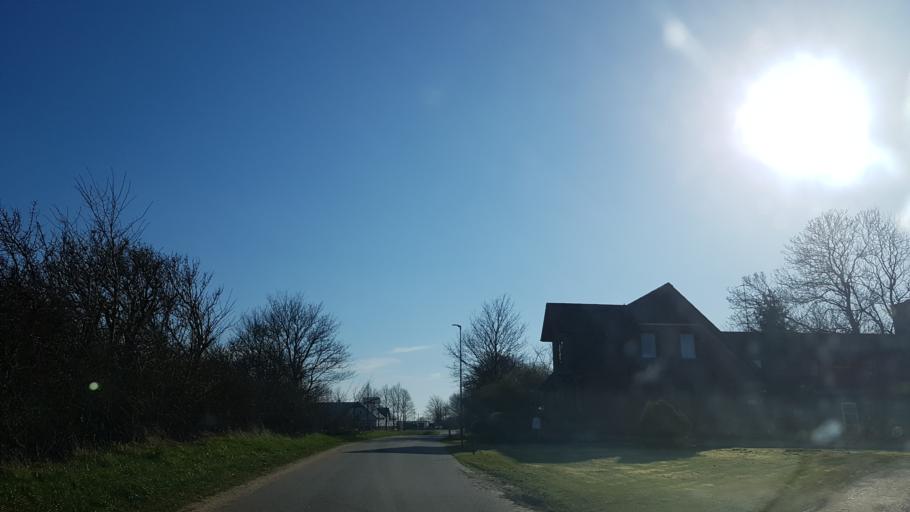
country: DK
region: South Denmark
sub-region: Vejen Kommune
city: Vejen
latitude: 55.4371
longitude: 9.1817
